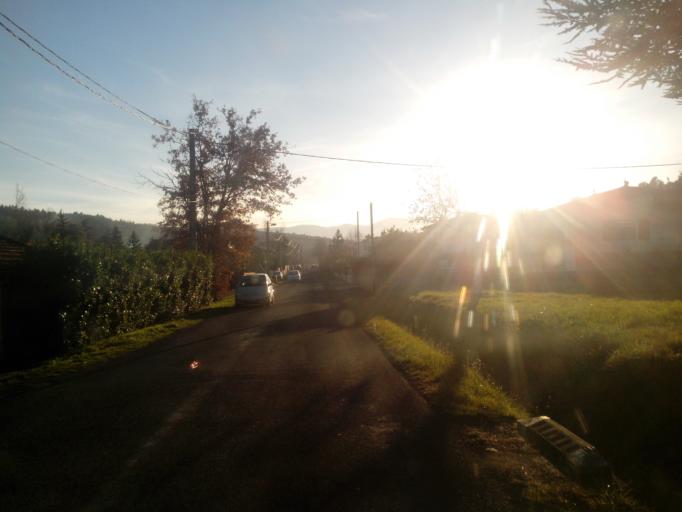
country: FR
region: Languedoc-Roussillon
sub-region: Departement de l'Aude
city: Esperaza
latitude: 42.9403
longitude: 2.2344
